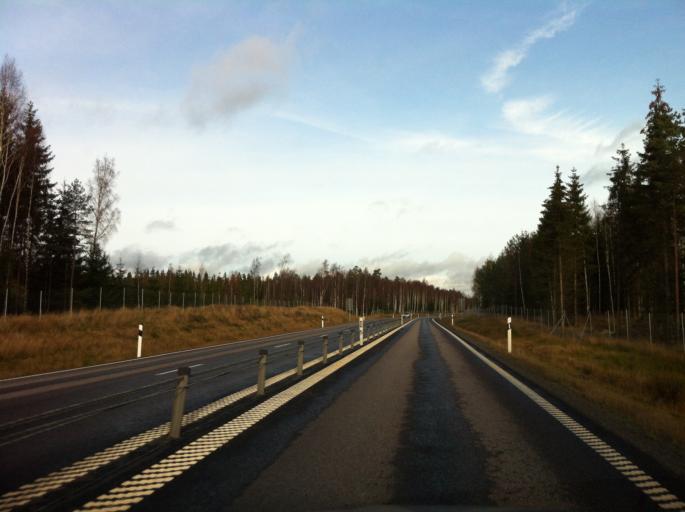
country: SE
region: Kronoberg
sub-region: Almhults Kommun
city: AElmhult
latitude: 56.6184
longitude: 14.2384
